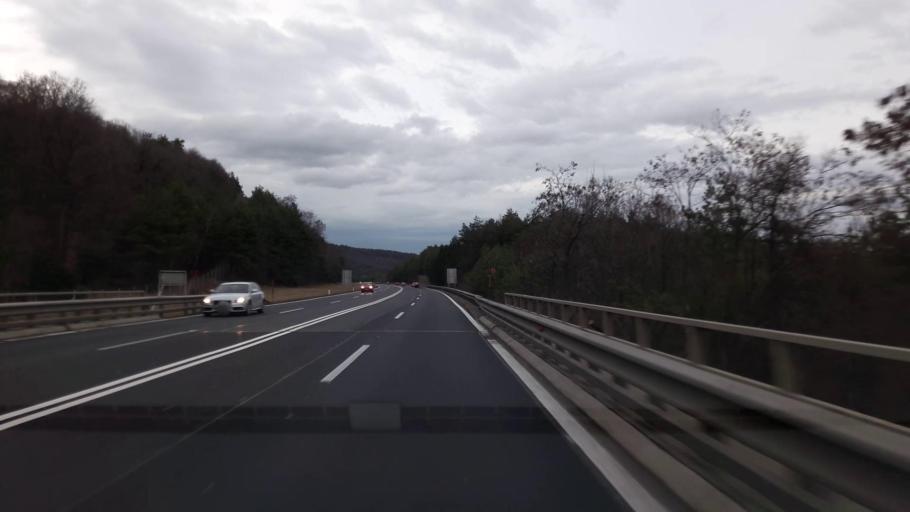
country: AT
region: Burgenland
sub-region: Politischer Bezirk Mattersburg
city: Sieggraben
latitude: 47.6870
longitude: 16.3835
